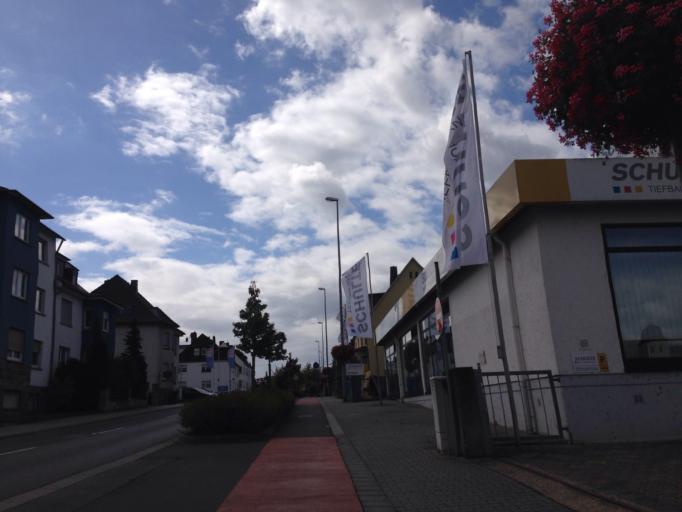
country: DE
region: Hesse
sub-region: Regierungsbezirk Giessen
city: Limburg an der Lahn
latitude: 50.3740
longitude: 8.0356
